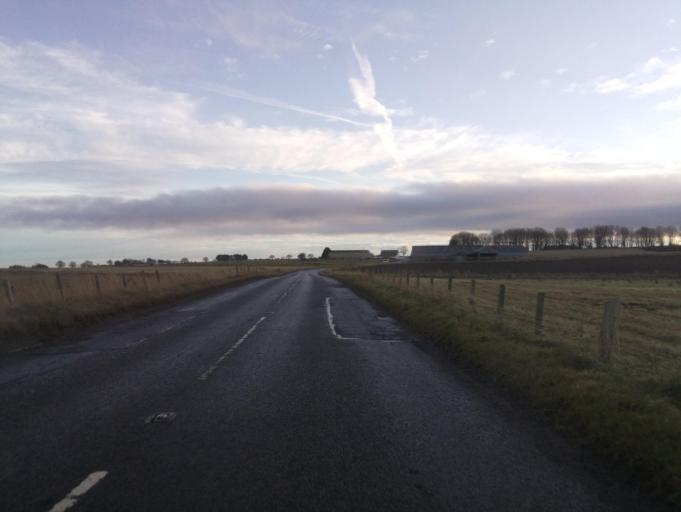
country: GB
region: Scotland
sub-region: Angus
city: Letham
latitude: 56.5709
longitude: -2.7793
